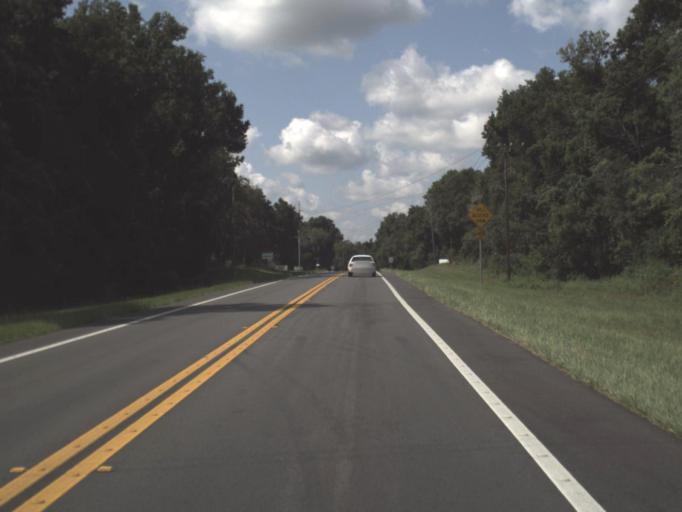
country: US
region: Florida
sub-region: Citrus County
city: Floral City
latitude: 28.7308
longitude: -82.3041
